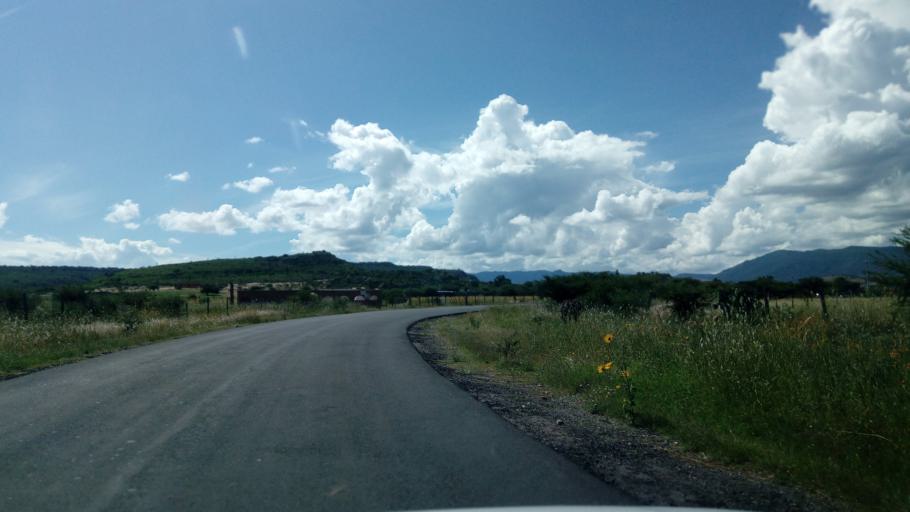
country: MX
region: Durango
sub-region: Durango
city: Jose Refugio Salcido
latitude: 23.8511
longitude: -104.4740
